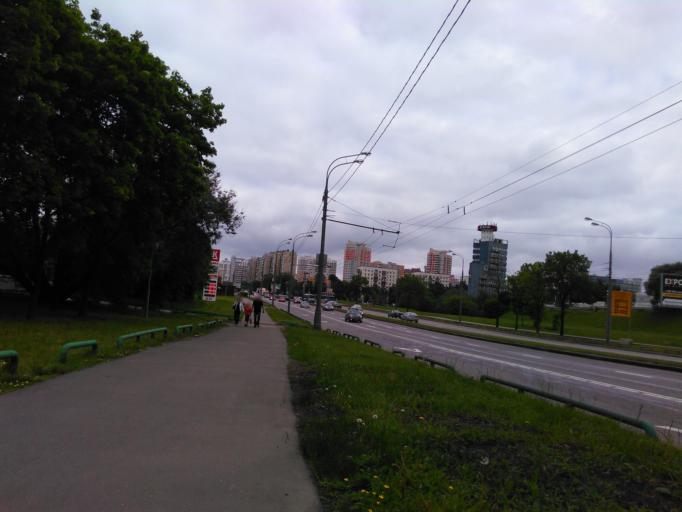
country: RU
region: Moscow
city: Troparevo
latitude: 55.6688
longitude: 37.4913
